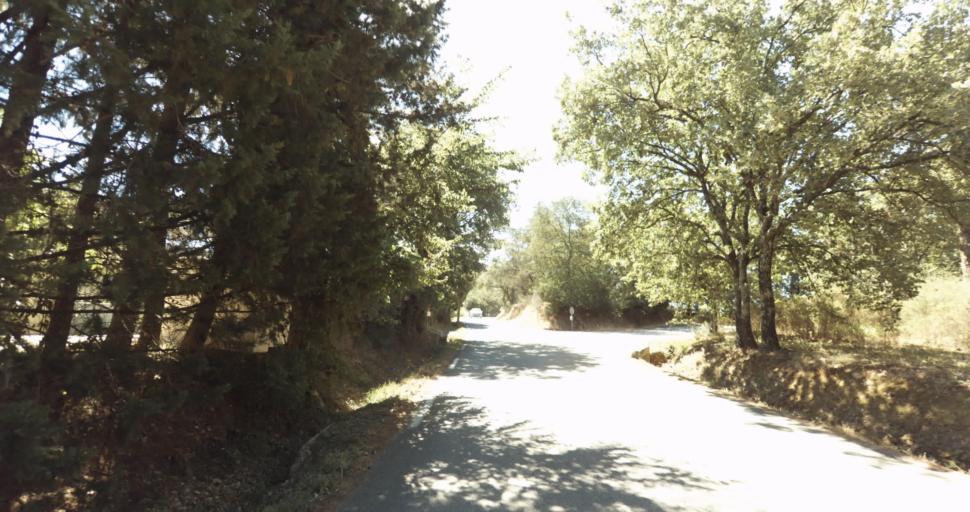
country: FR
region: Provence-Alpes-Cote d'Azur
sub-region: Departement du Var
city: Gassin
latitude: 43.2342
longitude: 6.5766
